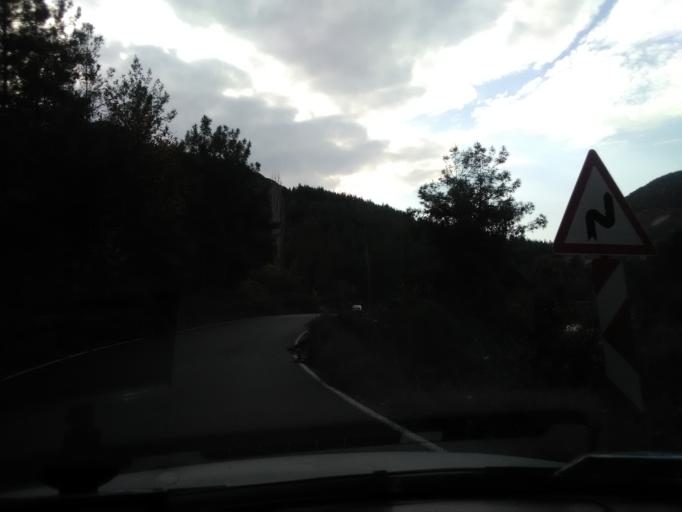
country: TR
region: Antalya
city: Gazipasa
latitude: 36.2860
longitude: 32.3736
